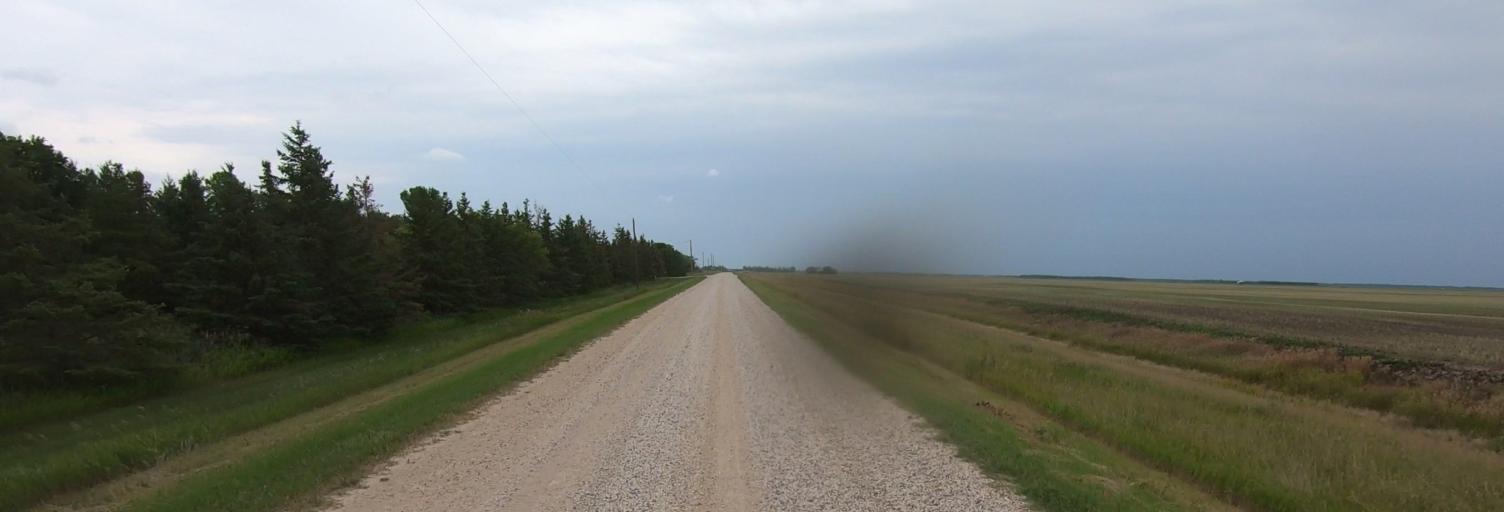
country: CA
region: Manitoba
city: Headingley
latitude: 49.7566
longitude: -97.4136
